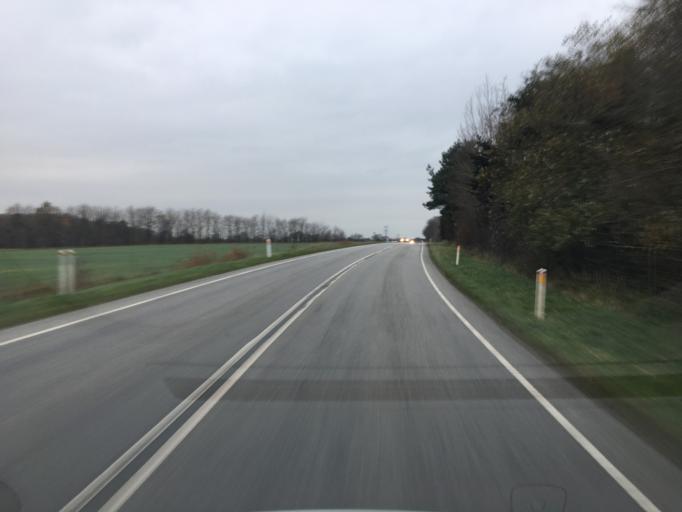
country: DK
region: South Denmark
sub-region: Aabenraa Kommune
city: Tinglev
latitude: 54.9973
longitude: 9.2331
